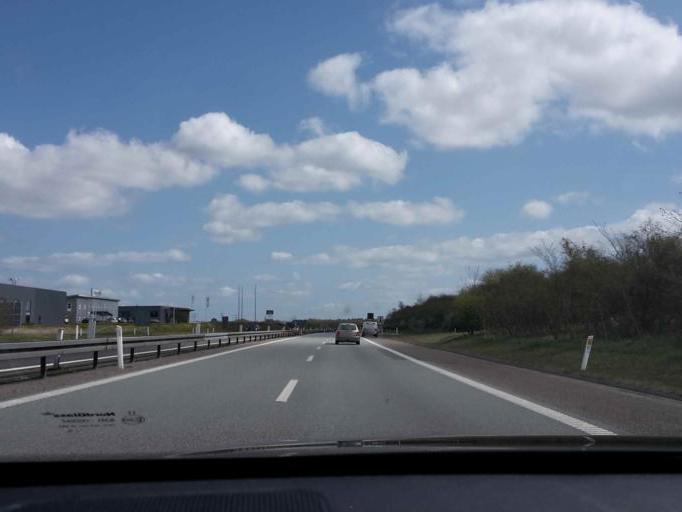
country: DK
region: South Denmark
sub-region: Vejen Kommune
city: Holsted
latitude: 55.5220
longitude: 8.9022
